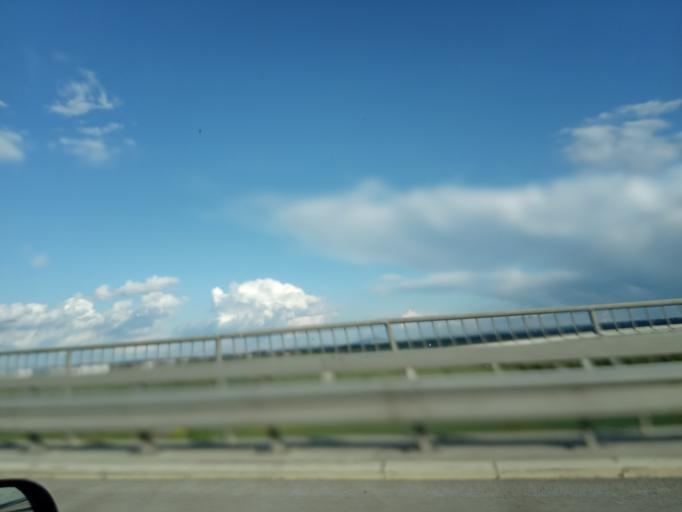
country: RS
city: Novi Banovci
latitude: 44.8894
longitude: 20.2887
